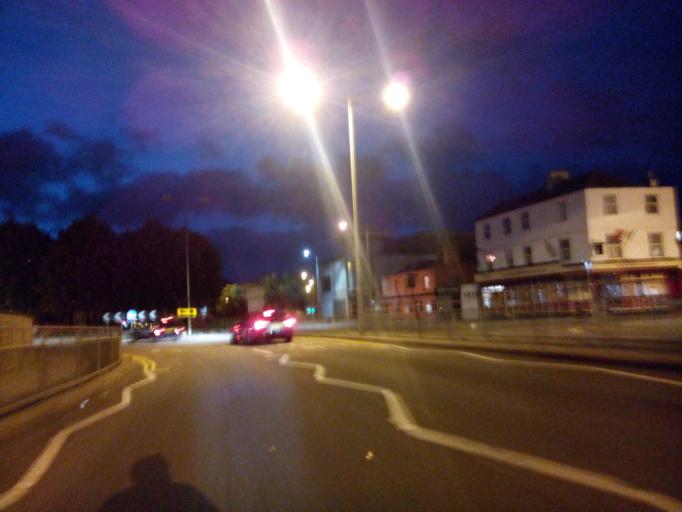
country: GB
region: England
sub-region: Kent
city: Dover
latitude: 51.1260
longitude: 1.3105
